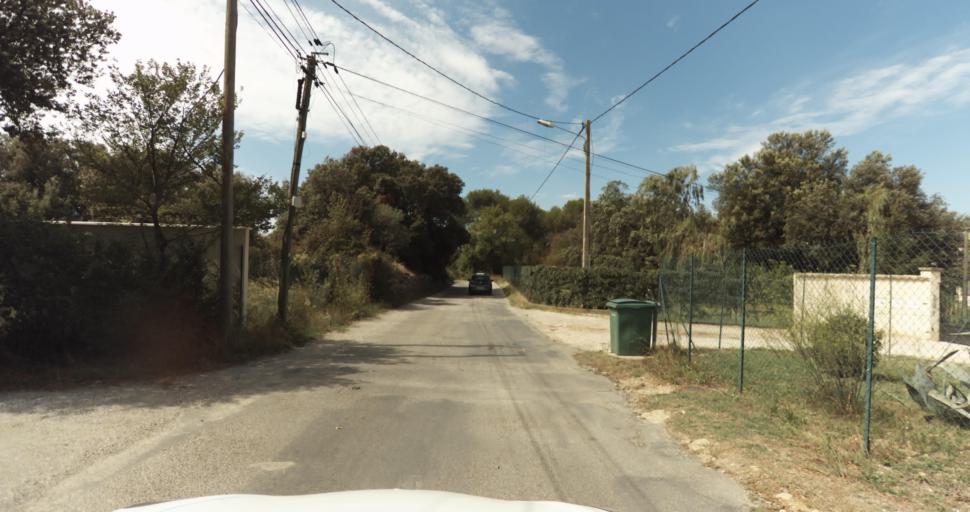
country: FR
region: Provence-Alpes-Cote d'Azur
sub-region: Departement des Bouches-du-Rhone
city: Miramas
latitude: 43.5889
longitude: 5.0218
